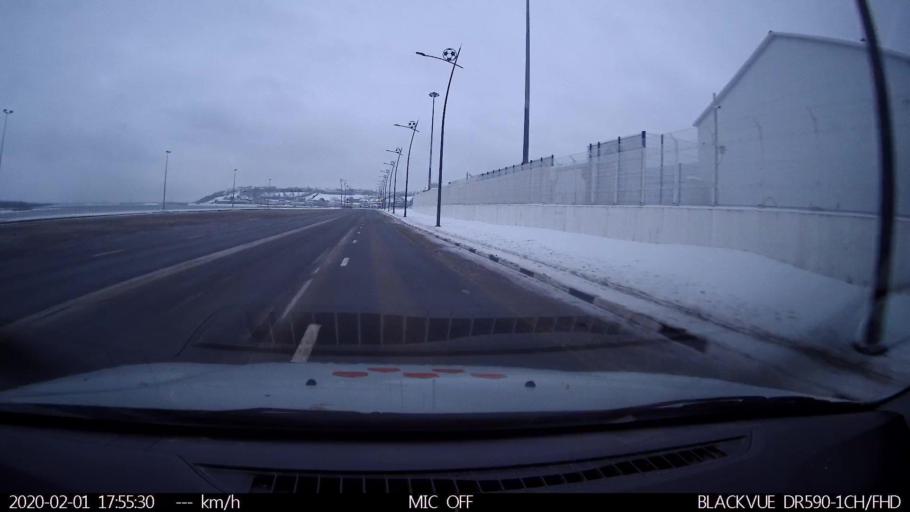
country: RU
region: Nizjnij Novgorod
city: Nizhniy Novgorod
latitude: 56.3391
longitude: 43.9675
